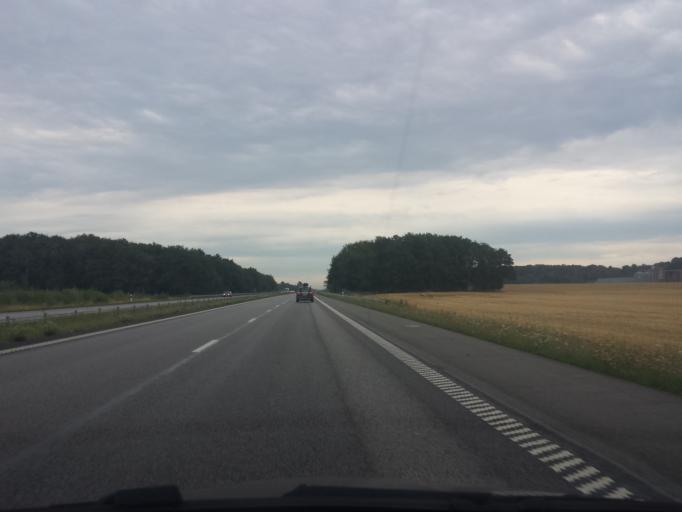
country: SE
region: Skane
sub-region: Malmo
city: Oxie
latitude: 55.5475
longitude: 13.1375
